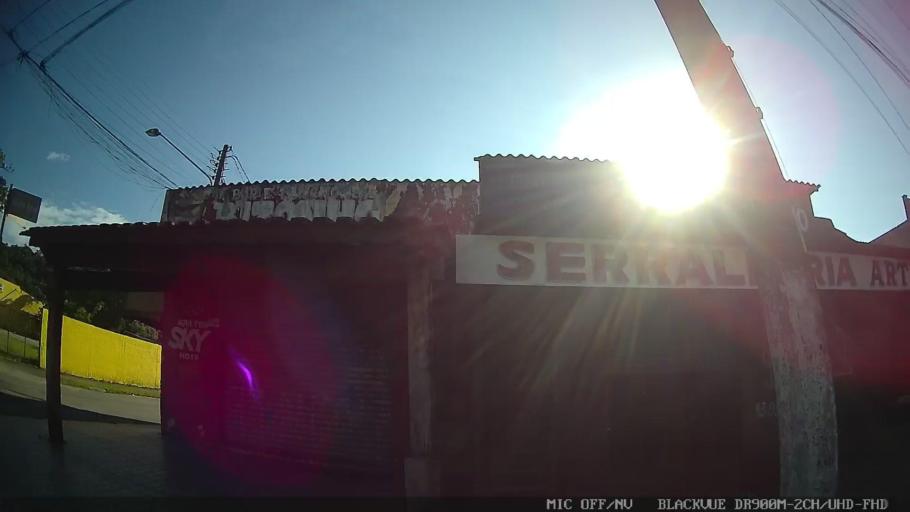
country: BR
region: Sao Paulo
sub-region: Peruibe
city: Peruibe
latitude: -24.2745
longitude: -46.9528
